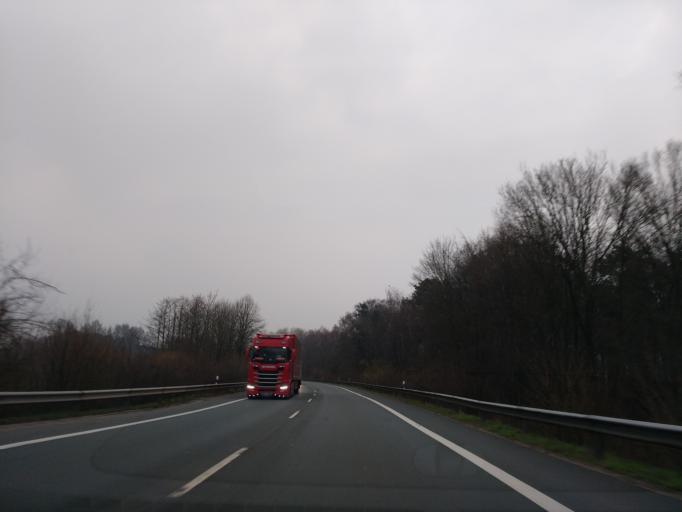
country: DE
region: North Rhine-Westphalia
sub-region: Regierungsbezirk Munster
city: Lotte
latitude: 52.3038
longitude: 7.9353
